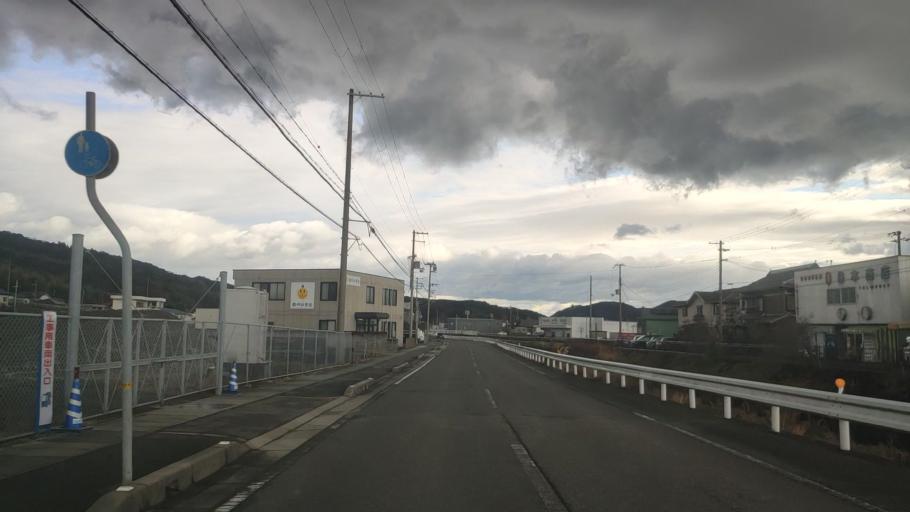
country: JP
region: Hyogo
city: Sumoto
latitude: 34.3320
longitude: 134.8666
